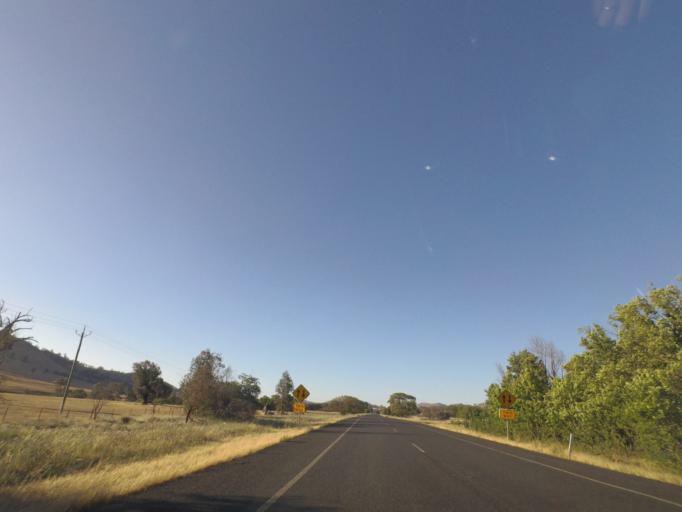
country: AU
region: New South Wales
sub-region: Gundagai
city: Gundagai
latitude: -34.9374
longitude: 148.1675
